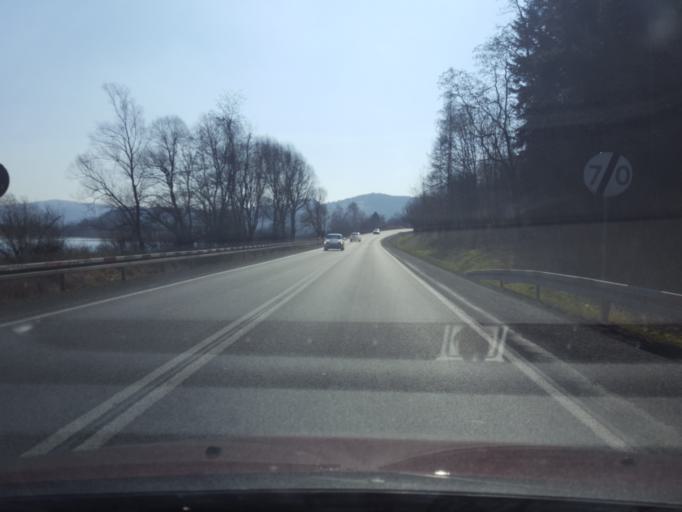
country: PL
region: Lesser Poland Voivodeship
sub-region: Powiat nowosadecki
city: Lososina Dolna
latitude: 49.7942
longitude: 20.6453
